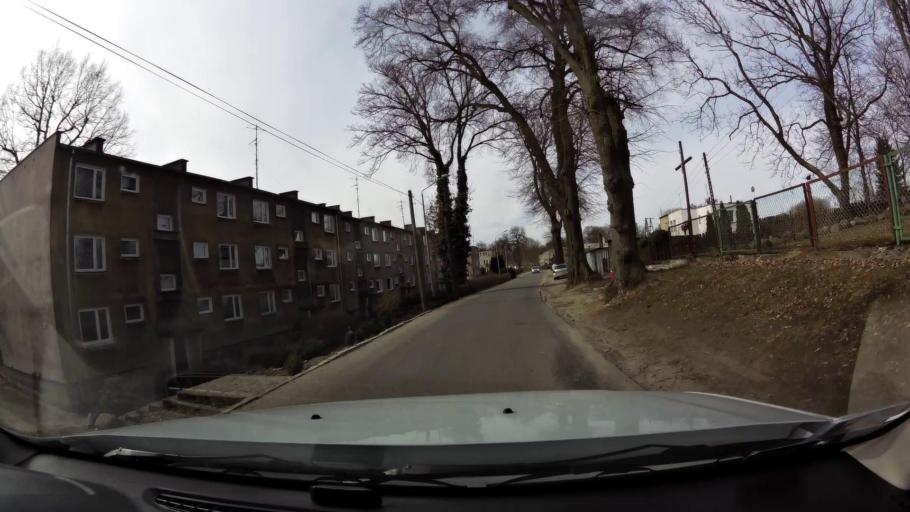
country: PL
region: West Pomeranian Voivodeship
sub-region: Powiat drawski
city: Drawsko Pomorskie
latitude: 53.5154
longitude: 15.7532
